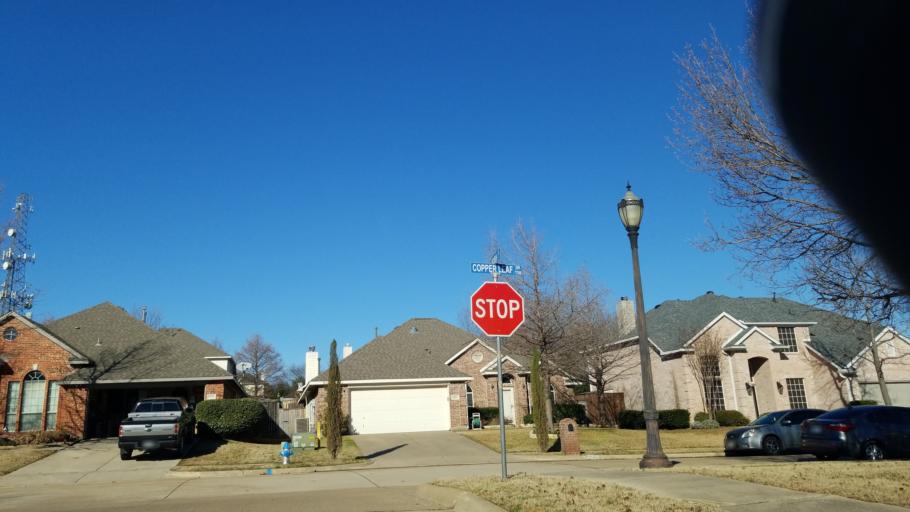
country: US
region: Texas
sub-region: Denton County
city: Corinth
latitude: 33.1427
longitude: -97.0832
